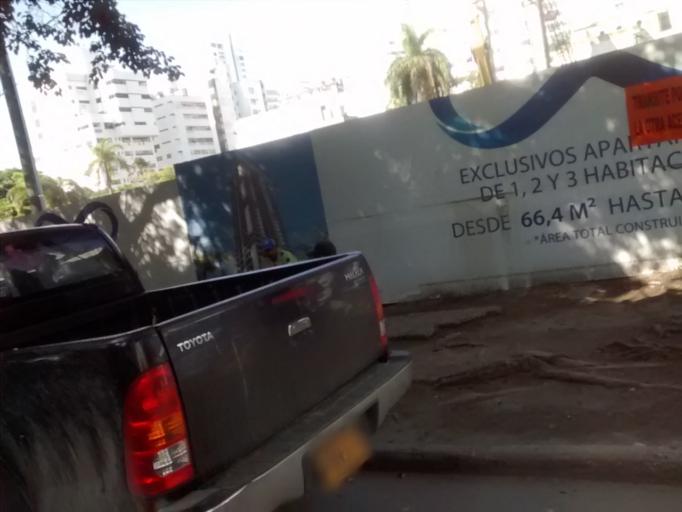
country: CO
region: Bolivar
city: Cartagena
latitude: 10.4029
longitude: -75.5540
